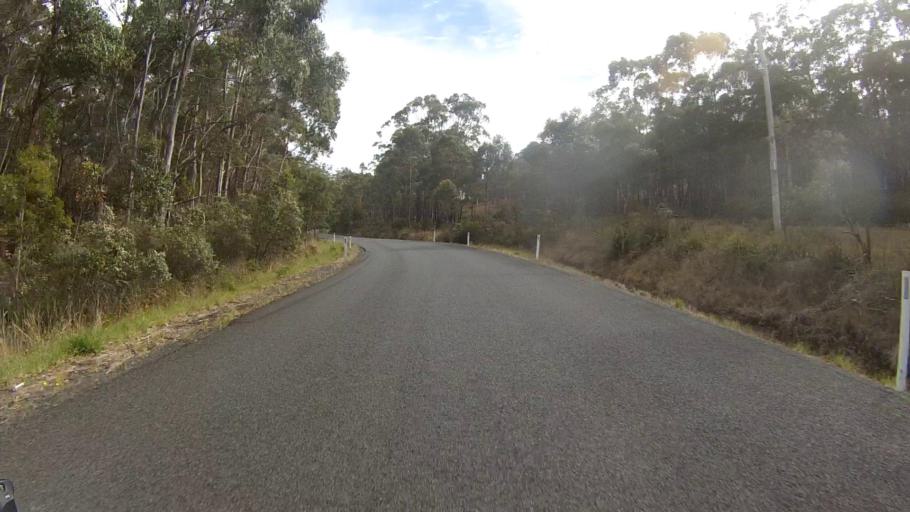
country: AU
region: Tasmania
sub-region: Sorell
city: Sorell
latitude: -42.8146
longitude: 147.7921
